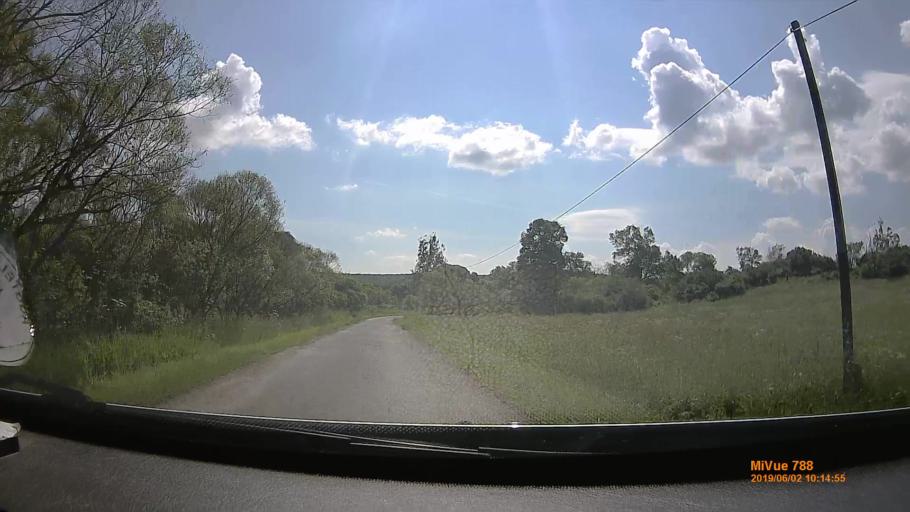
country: HU
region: Borsod-Abauj-Zemplen
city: Szendro
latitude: 48.5086
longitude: 20.7960
